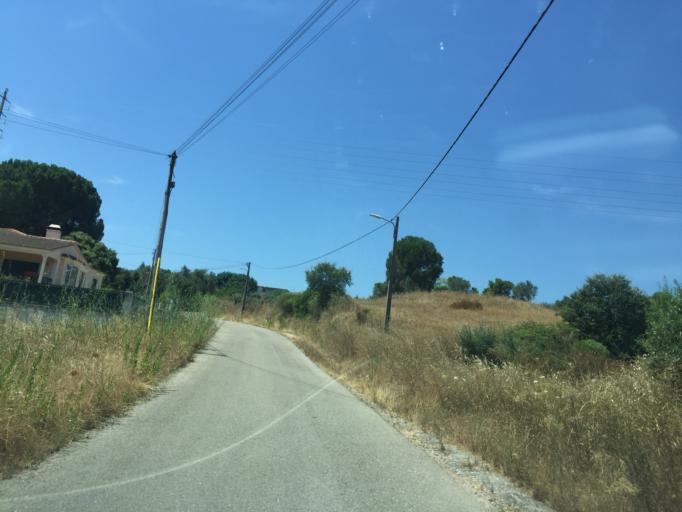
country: PT
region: Santarem
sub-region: Tomar
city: Tomar
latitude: 39.5935
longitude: -8.3483
